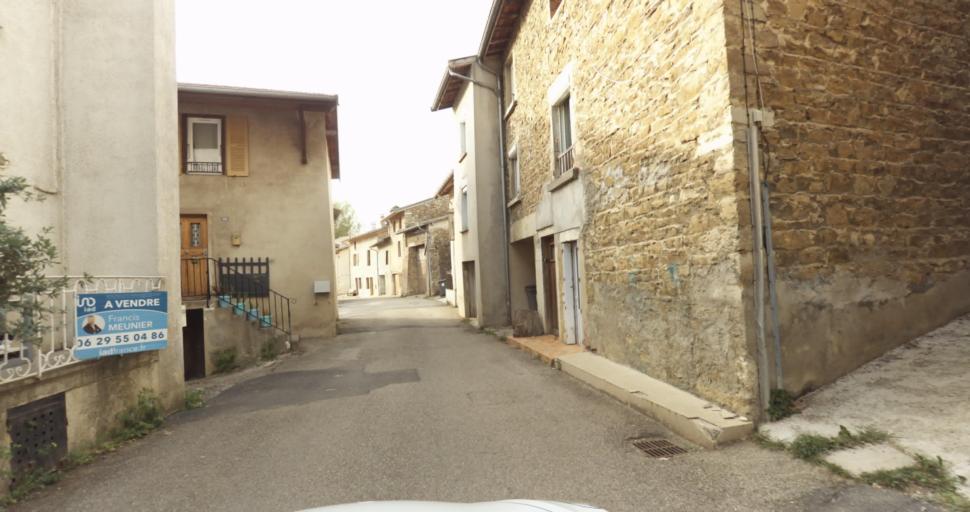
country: FR
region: Rhone-Alpes
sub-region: Departement de l'Ain
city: Amberieu-en-Bugey
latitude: 45.9554
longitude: 5.3739
